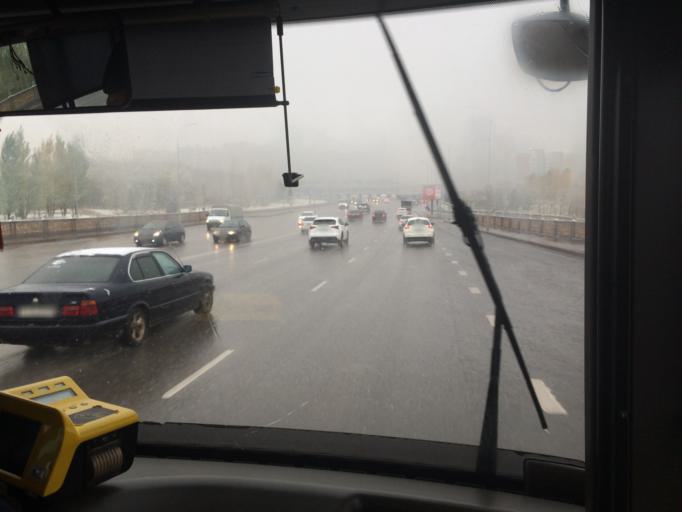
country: KZ
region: Astana Qalasy
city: Astana
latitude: 51.1358
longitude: 71.4417
